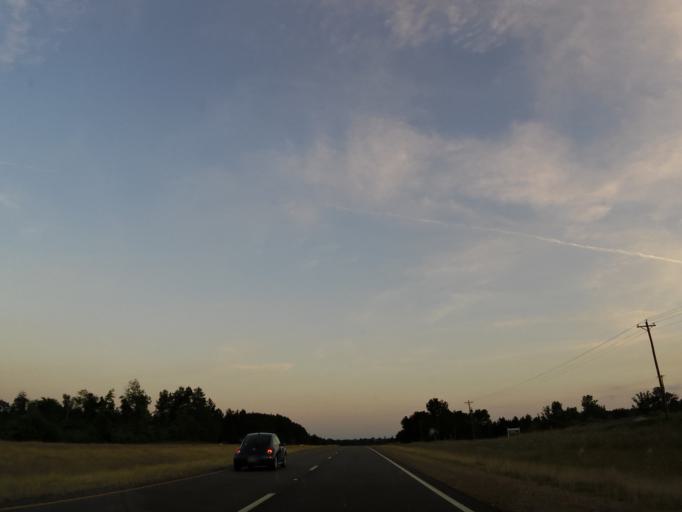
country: US
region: Mississippi
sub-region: Kemper County
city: De Kalb
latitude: 32.8143
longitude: -88.4572
